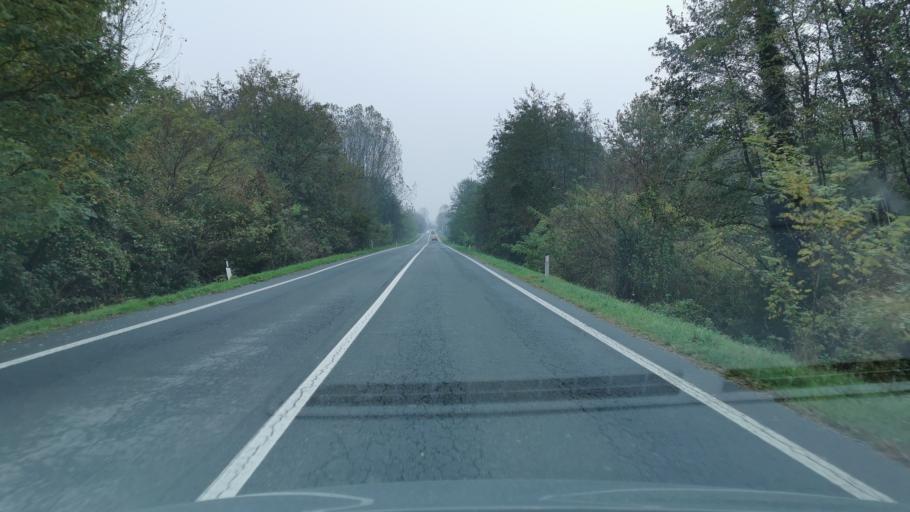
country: IT
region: Piedmont
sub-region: Provincia di Torino
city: Strambino
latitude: 45.3837
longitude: 7.8993
